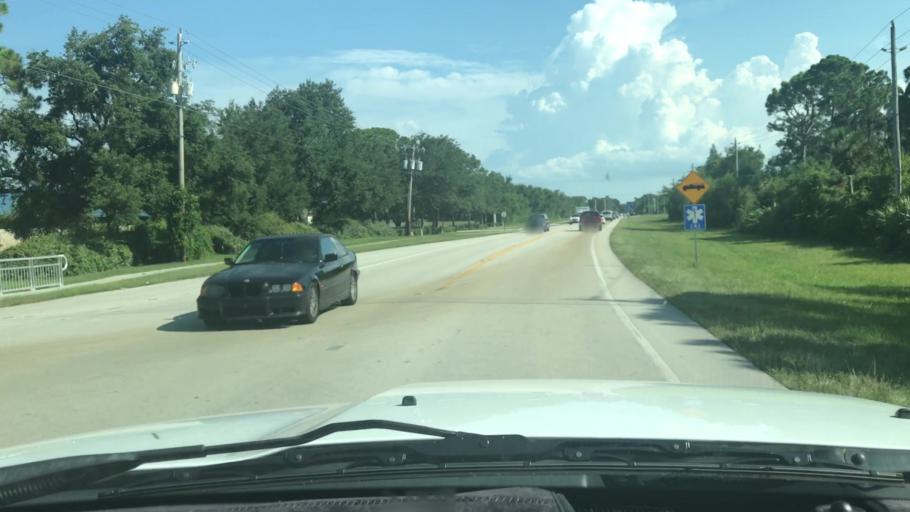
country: US
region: Florida
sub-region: Indian River County
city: Gifford
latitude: 27.6506
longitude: -80.4301
